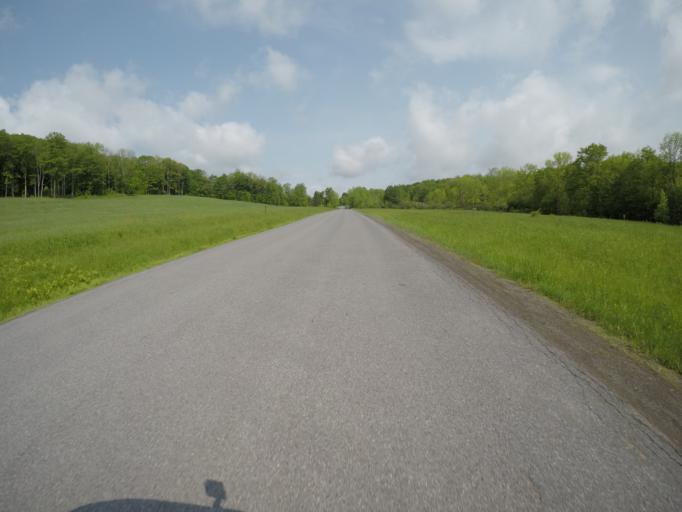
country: US
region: New York
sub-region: Delaware County
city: Stamford
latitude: 42.1637
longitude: -74.6642
